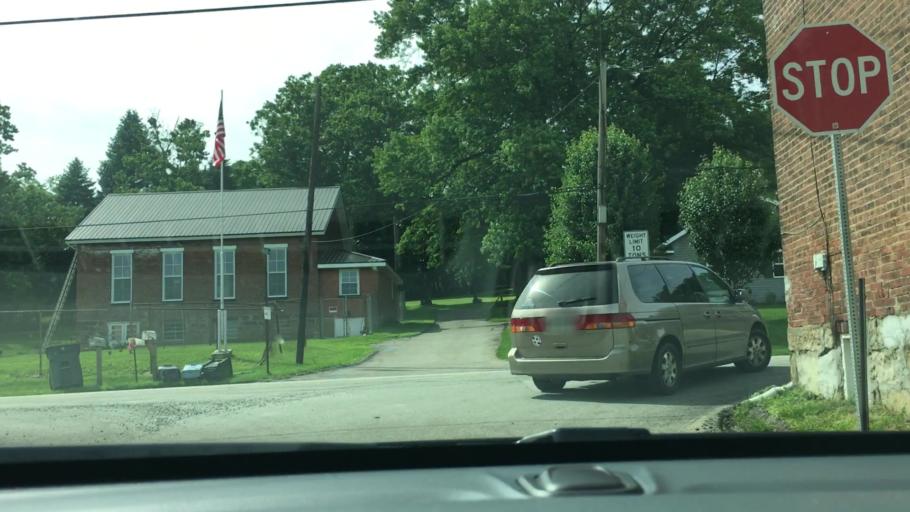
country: US
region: Pennsylvania
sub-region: Westmoreland County
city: New Stanton
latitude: 40.2620
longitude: -79.6199
